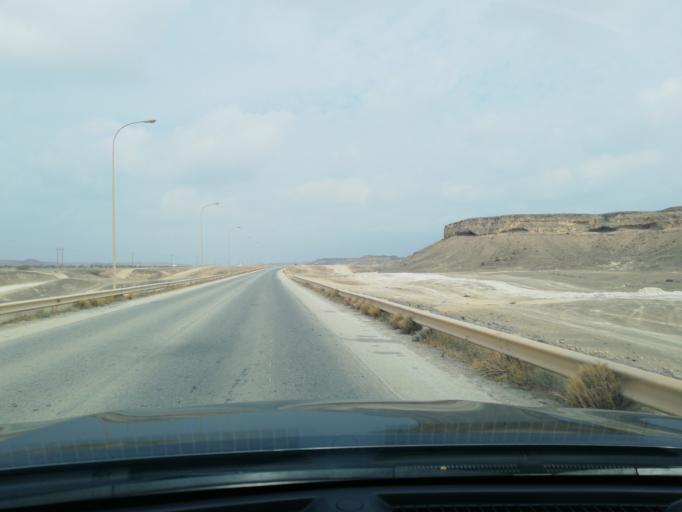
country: OM
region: Zufar
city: Salalah
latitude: 16.9535
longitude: 53.9211
